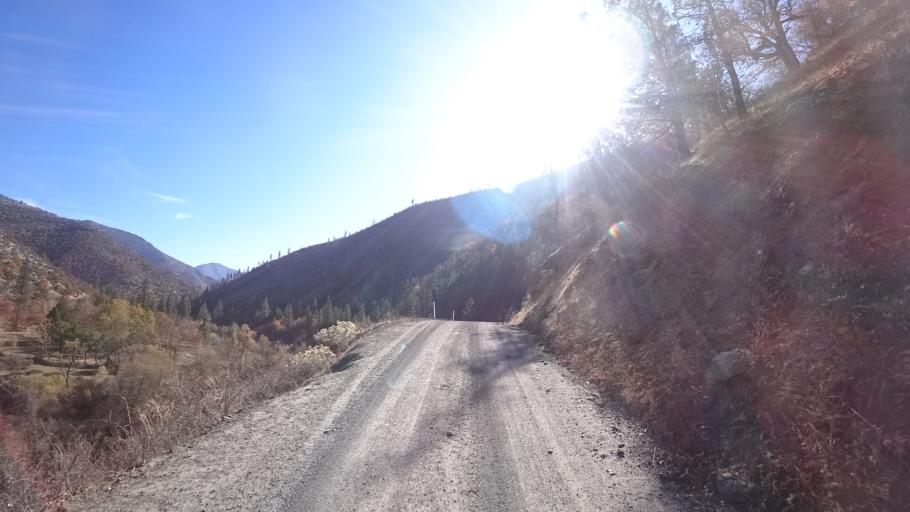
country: US
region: California
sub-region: Siskiyou County
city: Yreka
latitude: 41.8493
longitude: -122.6945
